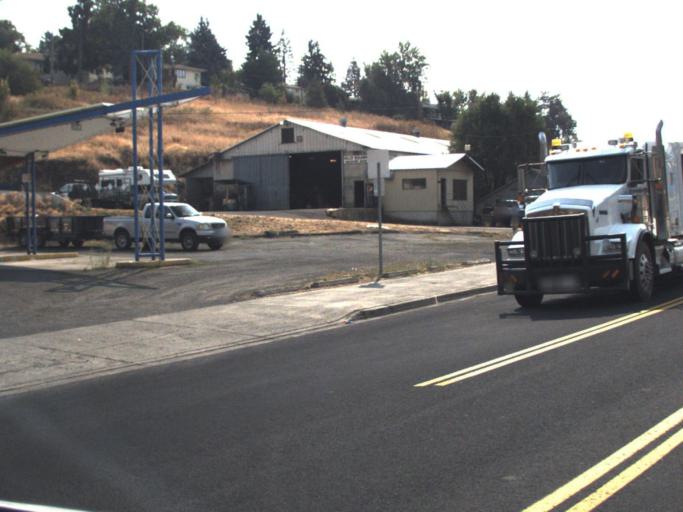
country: US
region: Washington
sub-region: Whitman County
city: Pullman
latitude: 46.7249
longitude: -117.1858
